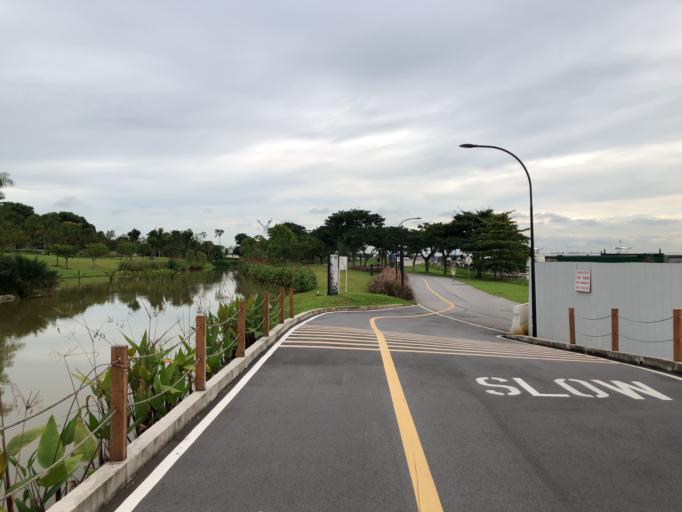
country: SG
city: Singapore
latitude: 1.2840
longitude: 103.8722
